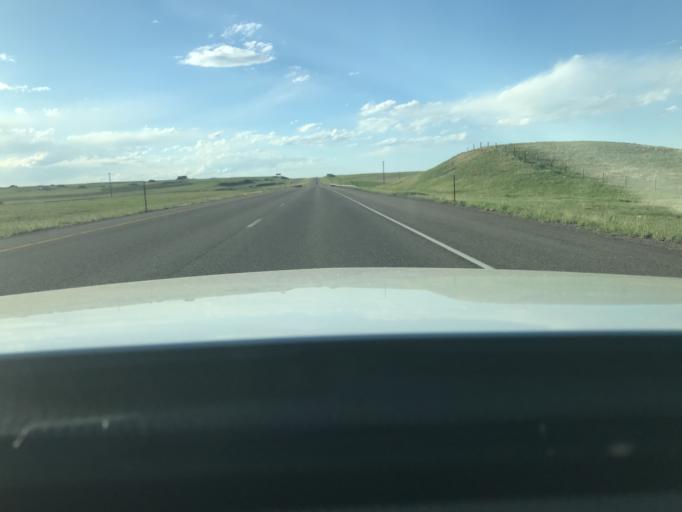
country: US
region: Wyoming
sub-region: Laramie County
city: Ranchettes
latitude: 41.2591
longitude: -104.8401
